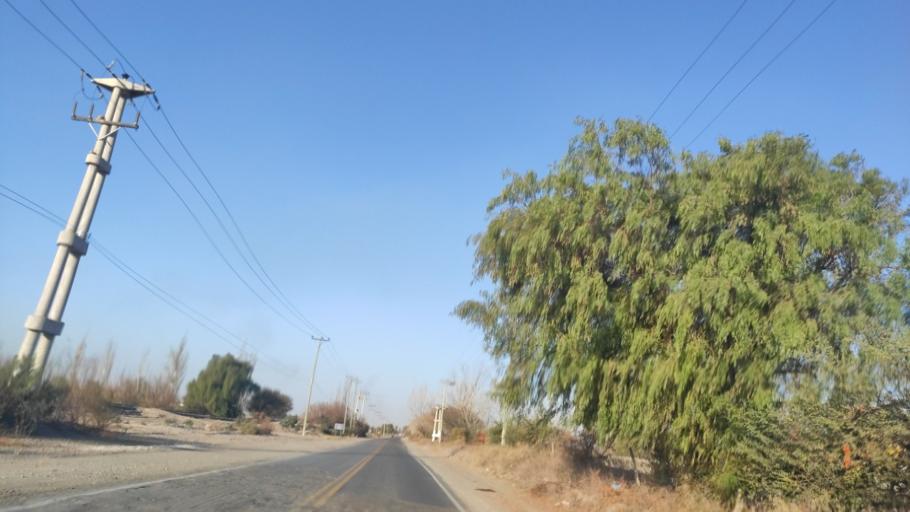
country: AR
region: San Juan
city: Villa Media Agua
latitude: -31.9792
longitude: -68.4555
